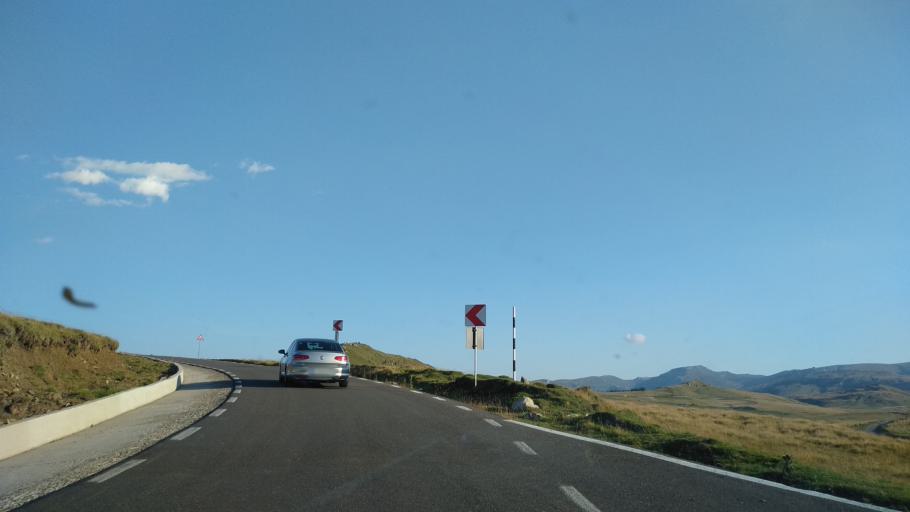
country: RO
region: Prahova
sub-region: Oras Busteni
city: Busteni
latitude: 45.3524
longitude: 25.4623
